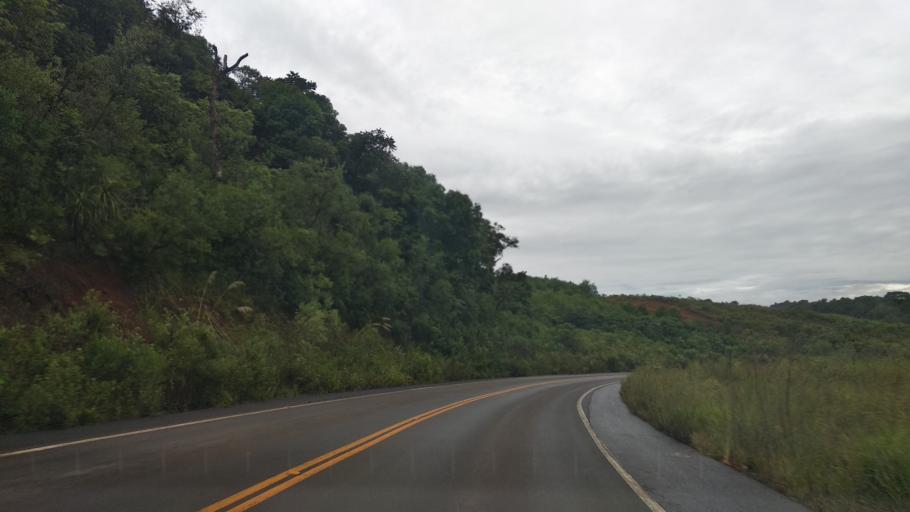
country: BR
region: Santa Catarina
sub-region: Videira
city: Videira
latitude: -27.0119
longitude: -51.1685
